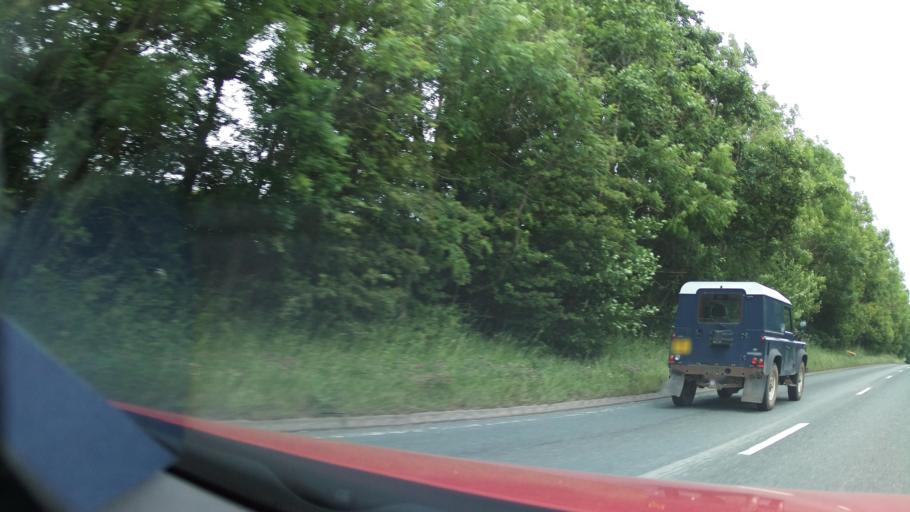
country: GB
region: England
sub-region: Staffordshire
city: Mayfield
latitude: 52.9929
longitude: -1.7483
